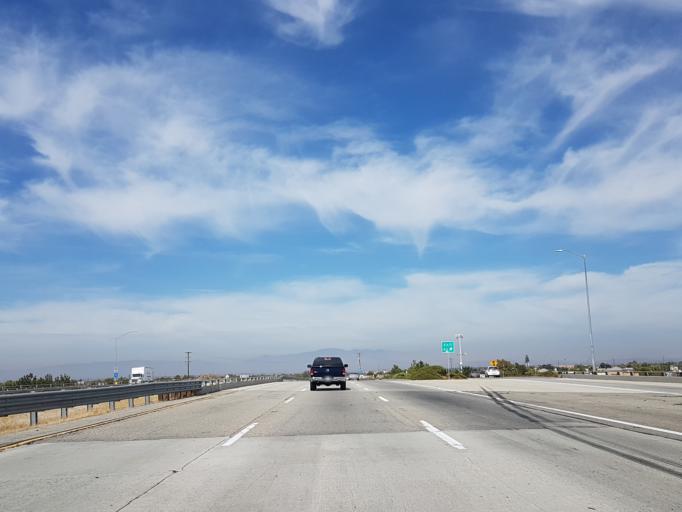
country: US
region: California
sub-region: Los Angeles County
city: Lancaster
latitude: 34.6819
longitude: -118.1638
